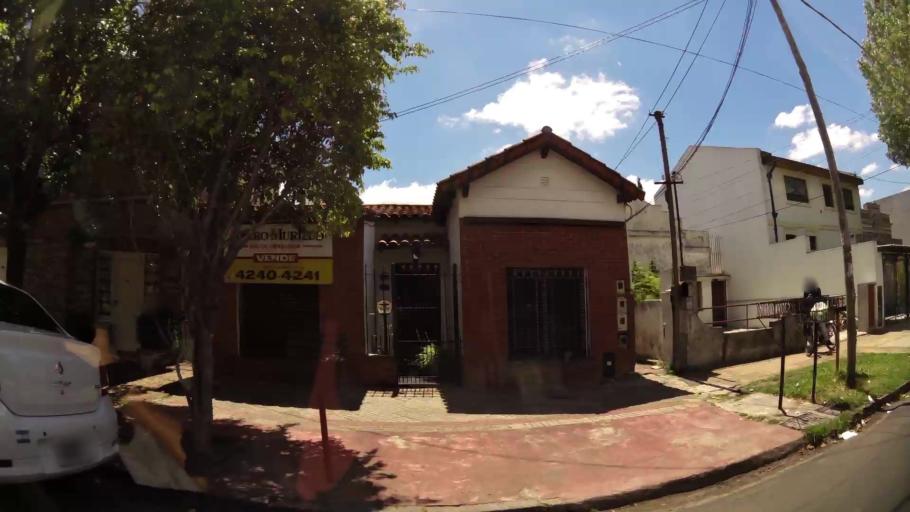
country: AR
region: Buenos Aires
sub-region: Partido de Lanus
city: Lanus
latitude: -34.7272
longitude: -58.4032
